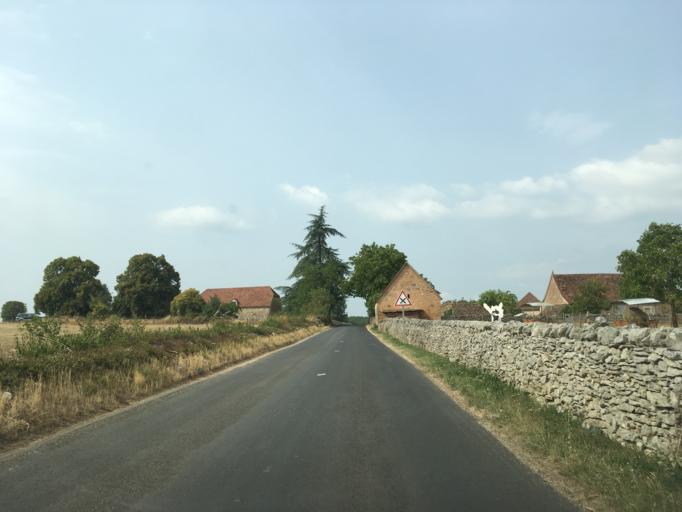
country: FR
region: Midi-Pyrenees
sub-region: Departement du Lot
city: Gramat
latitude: 44.8164
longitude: 1.6023
